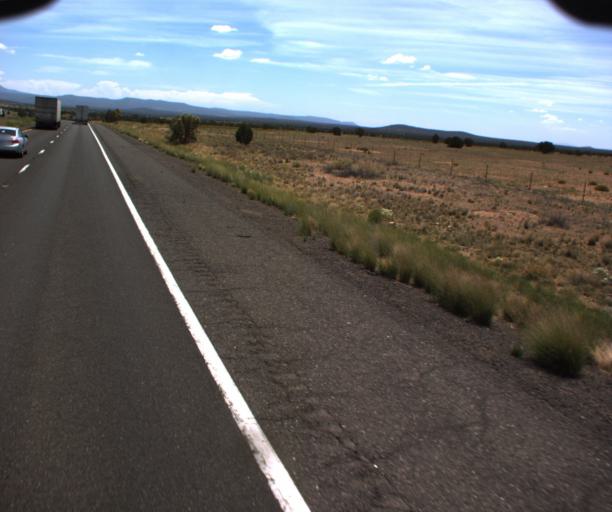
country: US
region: Arizona
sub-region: Yavapai County
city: Paulden
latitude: 35.2220
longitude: -112.5484
